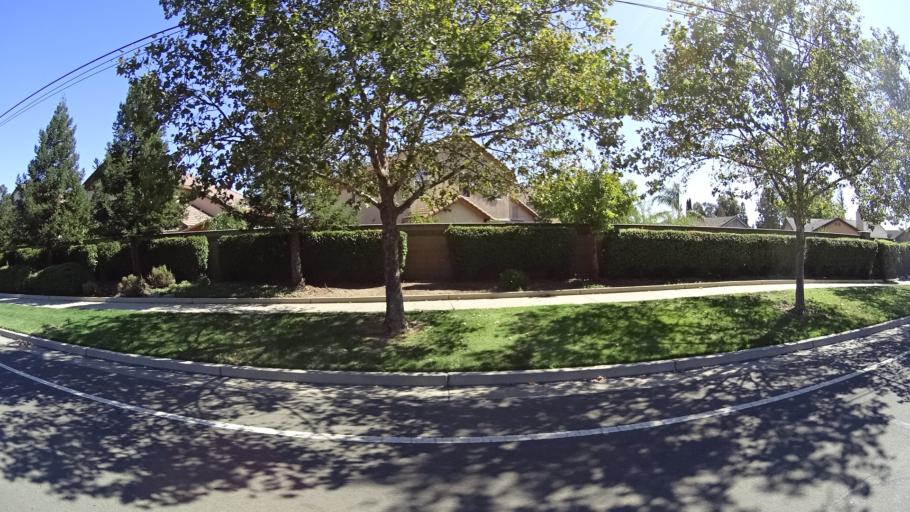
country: US
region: California
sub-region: Sacramento County
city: Vineyard
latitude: 38.4437
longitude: -121.3716
